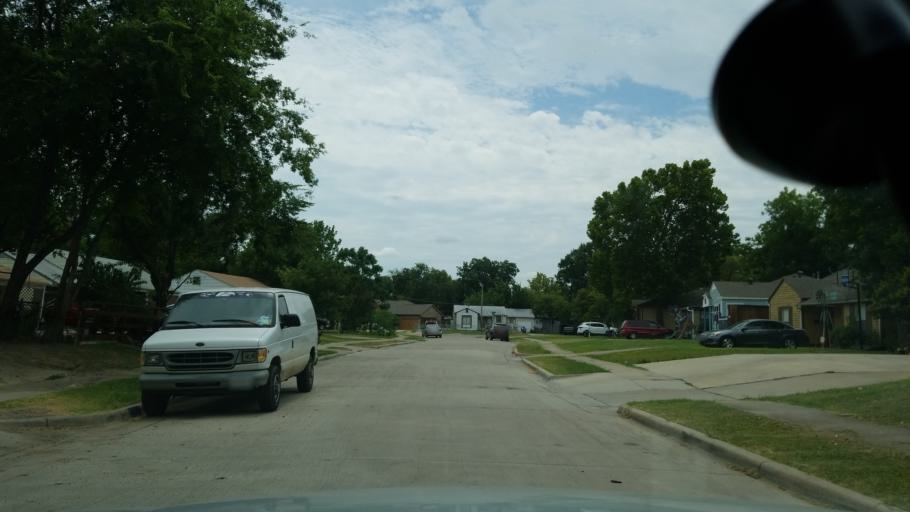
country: US
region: Texas
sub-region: Dallas County
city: Grand Prairie
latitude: 32.7386
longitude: -96.9891
